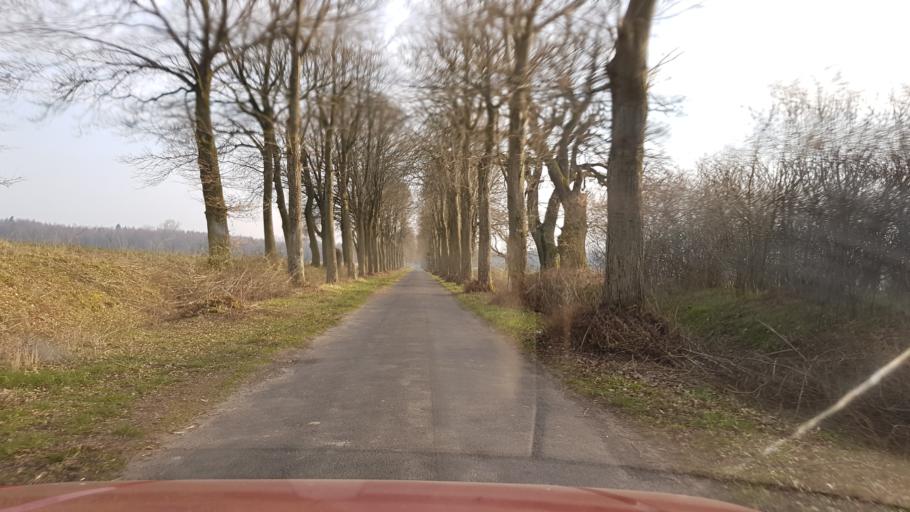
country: PL
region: West Pomeranian Voivodeship
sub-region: Powiat bialogardzki
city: Bialogard
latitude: 54.0871
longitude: 15.9748
